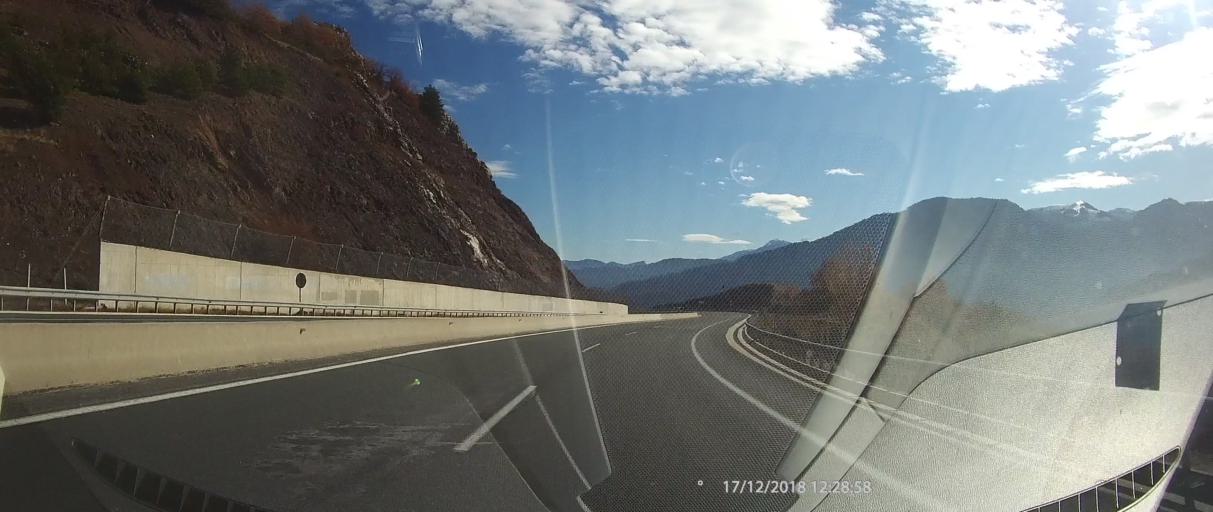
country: GR
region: Epirus
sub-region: Nomos Ioanninon
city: Metsovo
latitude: 39.7864
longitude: 21.2842
